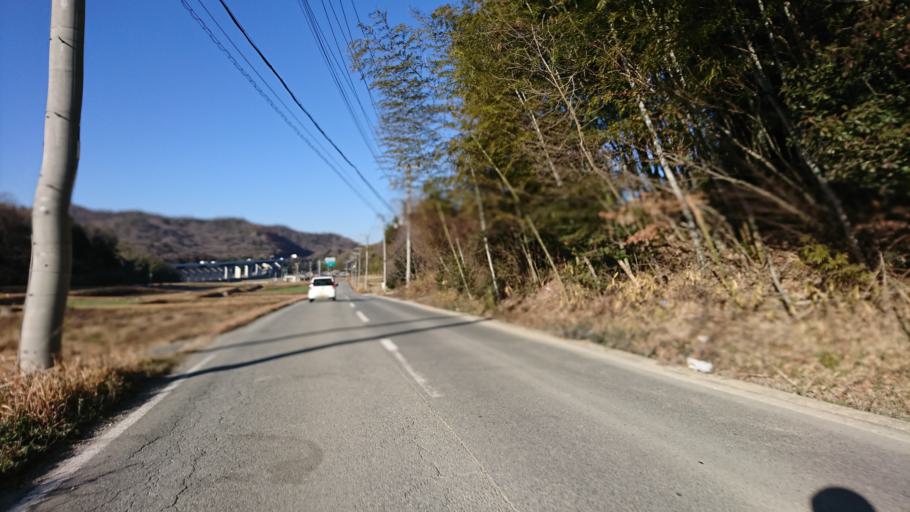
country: JP
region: Hyogo
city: Ono
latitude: 34.8394
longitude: 134.8713
